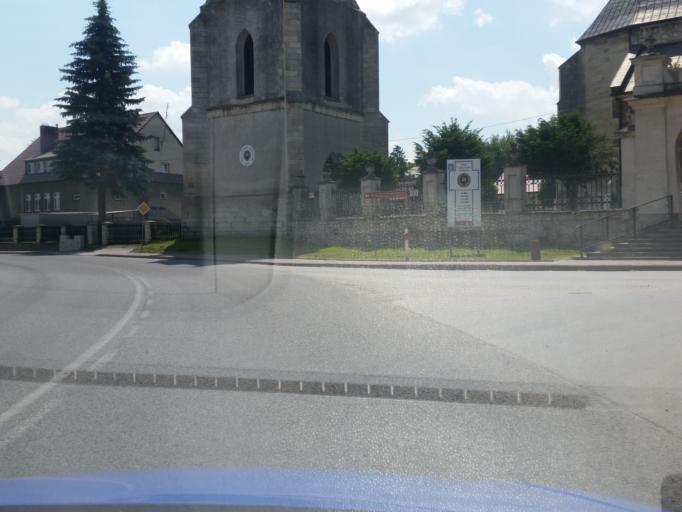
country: PL
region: Swietokrzyskie
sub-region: Powiat kazimierski
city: Skalbmierz
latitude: 50.3175
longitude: 20.3989
